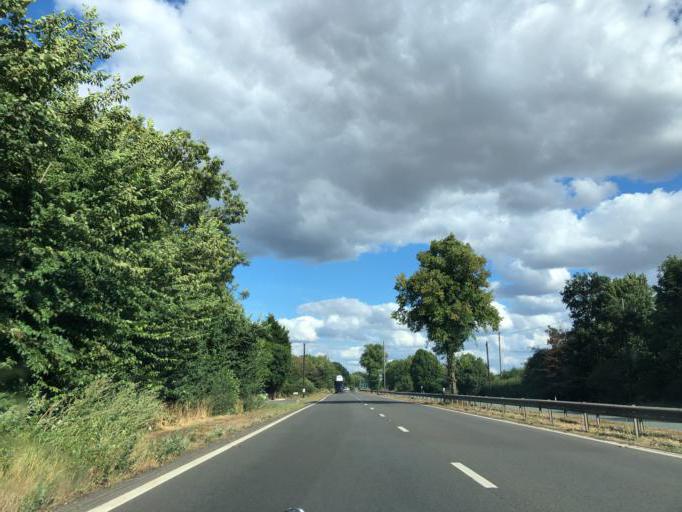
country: GB
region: England
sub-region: Warwickshire
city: Wolston
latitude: 52.3480
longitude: -1.3522
